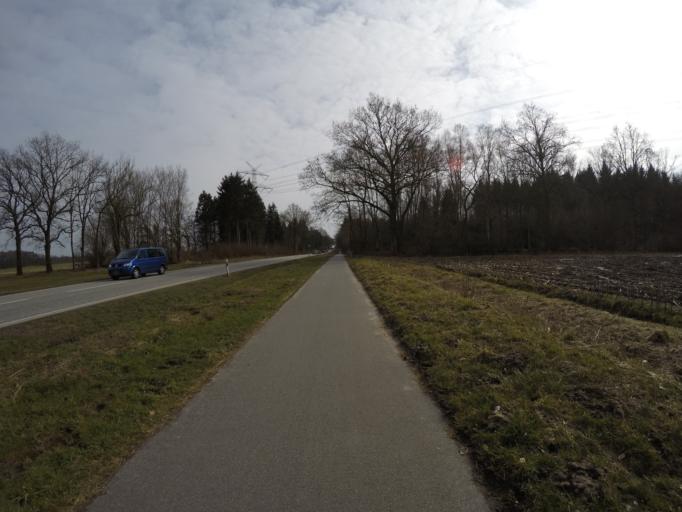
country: DE
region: Schleswig-Holstein
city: Bilsen
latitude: 53.7592
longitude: 9.8805
